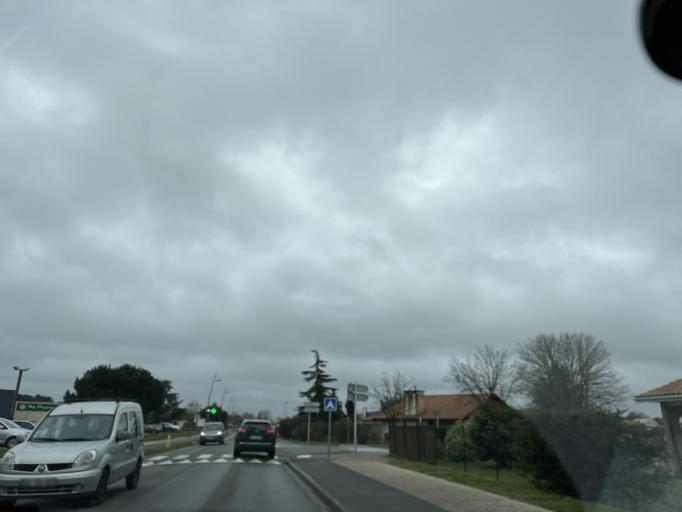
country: FR
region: Aquitaine
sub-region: Departement de la Gironde
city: Lesparre-Medoc
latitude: 45.3029
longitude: -0.9352
